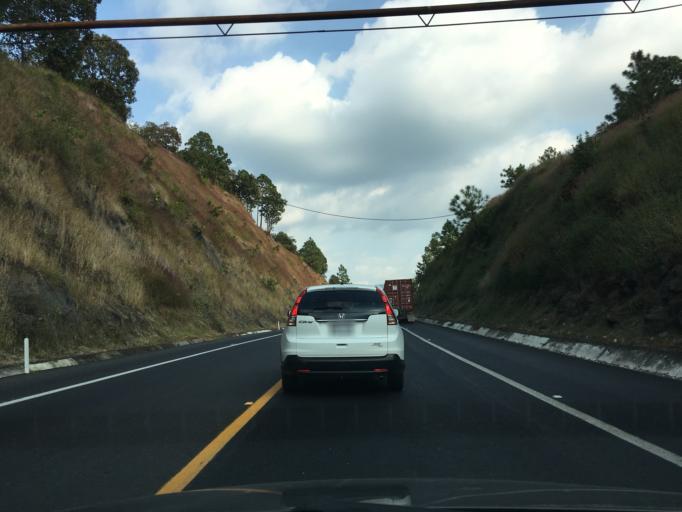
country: MX
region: Michoacan
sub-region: Ziracuaretiro
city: Patuan
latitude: 19.4340
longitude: -101.9041
